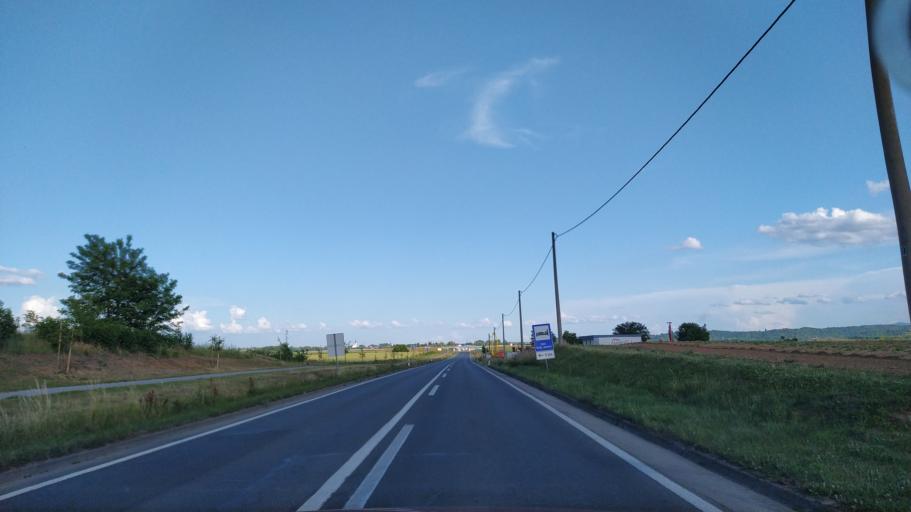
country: HR
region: Virovitick-Podravska
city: Spisic-Bukovica
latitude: 45.8468
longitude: 17.3420
